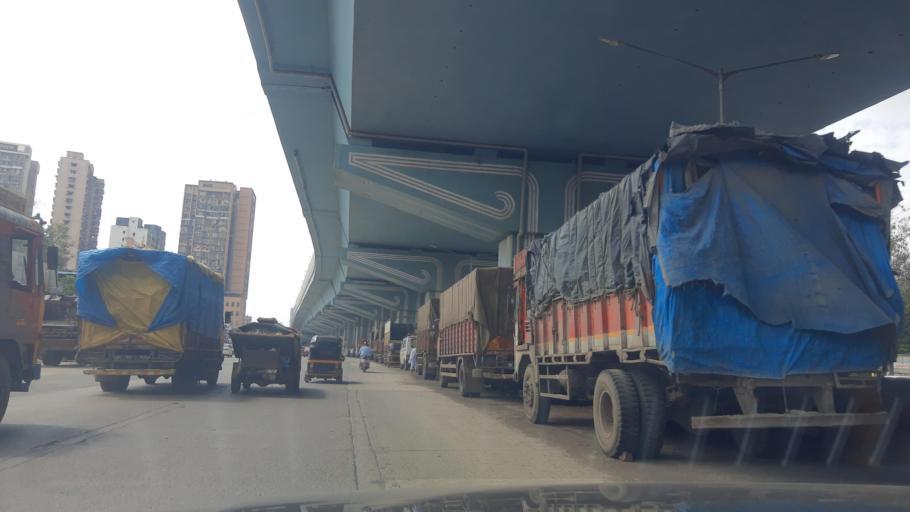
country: IN
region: Maharashtra
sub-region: Mumbai Suburban
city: Mumbai
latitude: 19.0608
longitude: 72.9208
